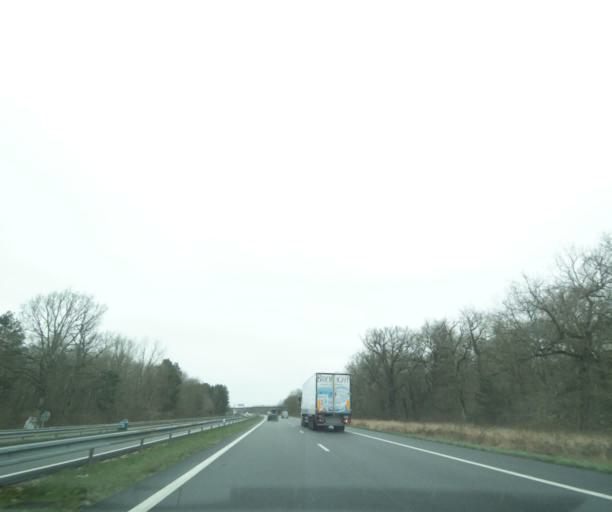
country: FR
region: Centre
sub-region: Departement du Loir-et-Cher
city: Salbris
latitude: 47.4448
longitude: 2.0062
